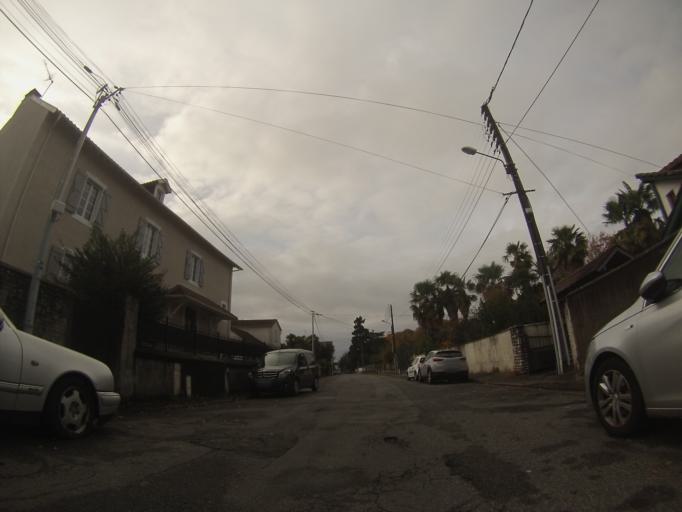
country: FR
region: Aquitaine
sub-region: Departement des Pyrenees-Atlantiques
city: Jurancon
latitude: 43.2869
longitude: -0.3824
